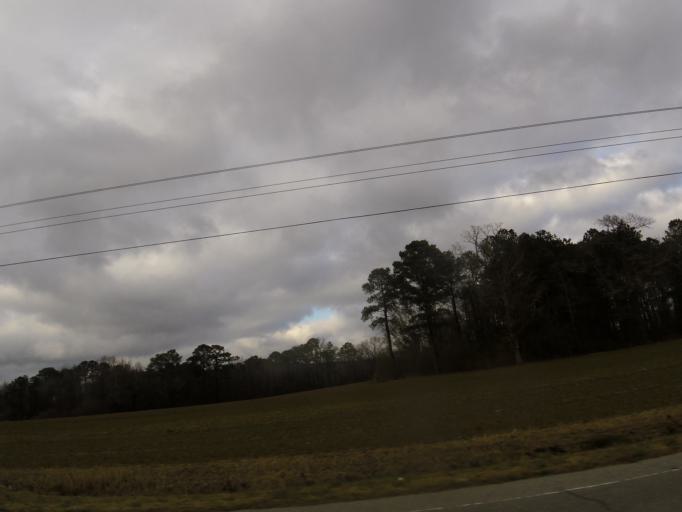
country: US
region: North Carolina
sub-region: Edgecombe County
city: Pinetops
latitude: 35.8539
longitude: -77.6777
